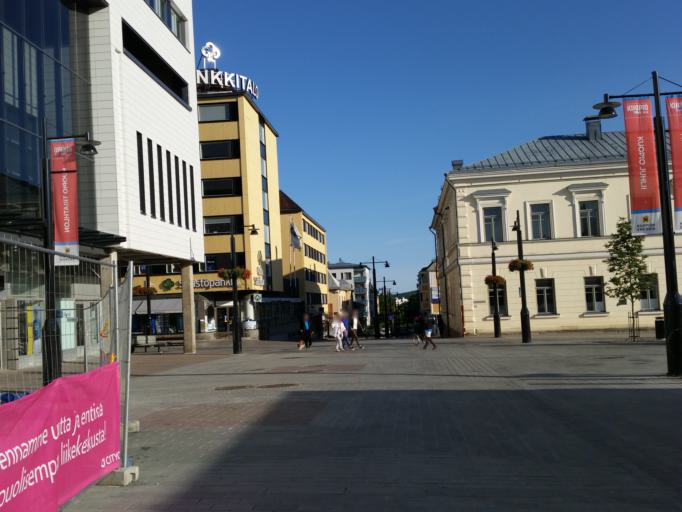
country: FI
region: Northern Savo
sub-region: Kuopio
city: Kuopio
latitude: 62.8921
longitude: 27.6797
